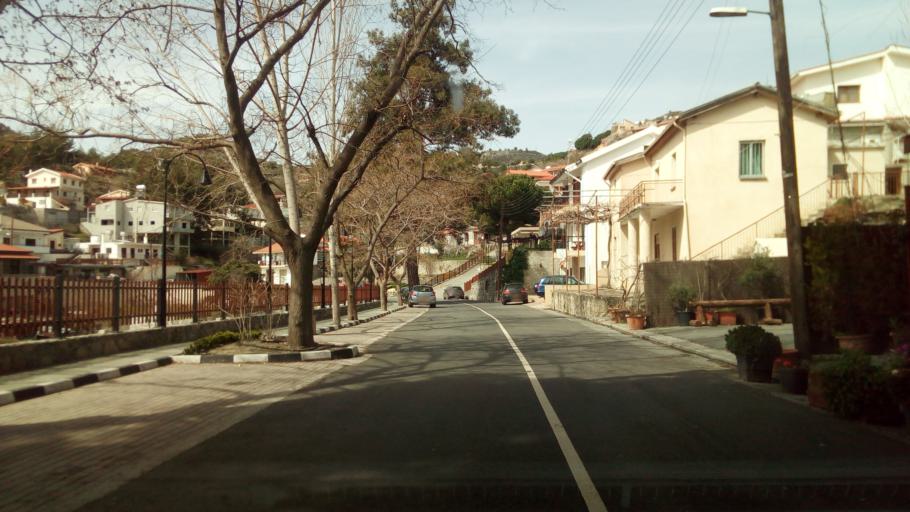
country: CY
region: Limassol
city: Kyperounta
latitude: 34.9173
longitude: 33.0170
